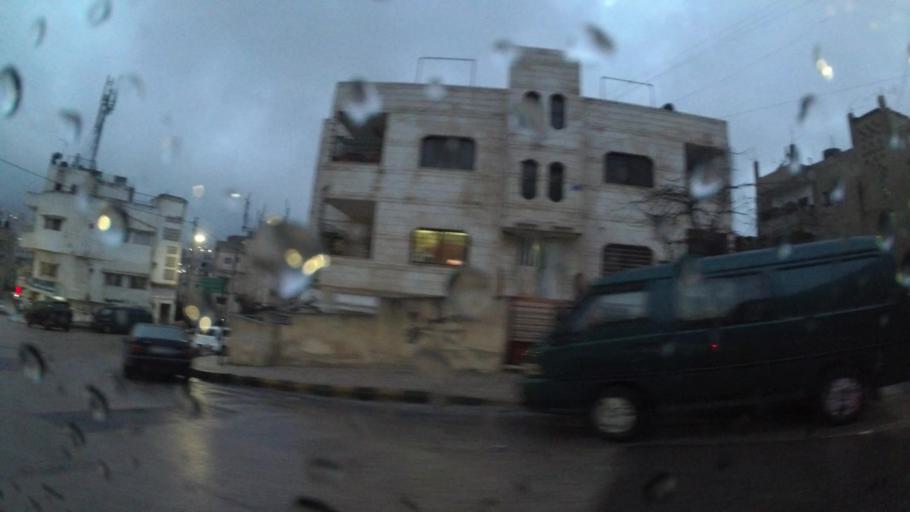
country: JO
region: Amman
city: Al Jubayhah
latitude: 32.0264
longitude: 35.8473
